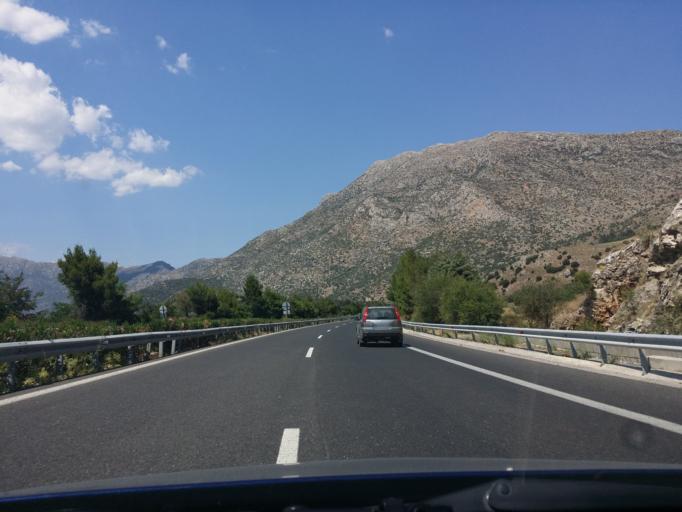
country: GR
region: Peloponnese
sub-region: Nomos Arkadias
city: Tripoli
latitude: 37.6170
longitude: 22.4585
